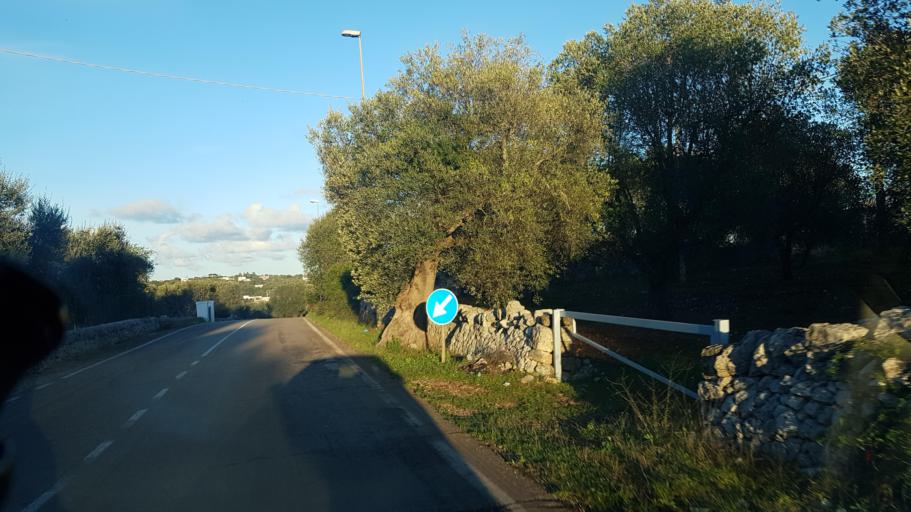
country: IT
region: Apulia
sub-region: Provincia di Brindisi
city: Ostuni
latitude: 40.7081
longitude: 17.5417
